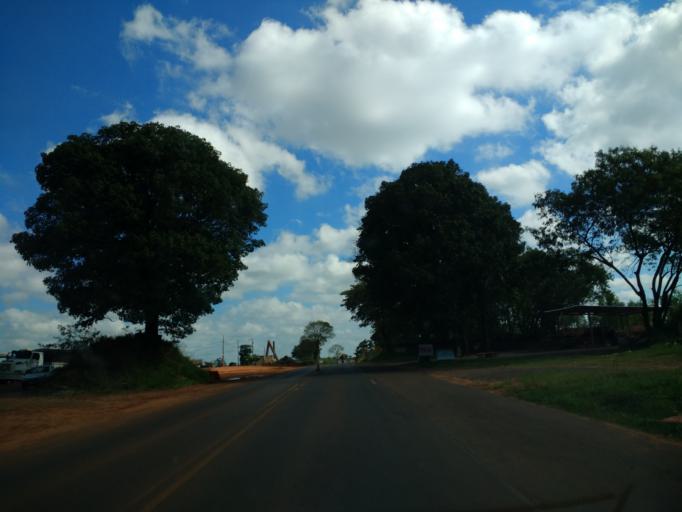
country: BR
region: Parana
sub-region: Alto Piquiri
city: Alto Piquiri
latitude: -23.8884
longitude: -53.4054
